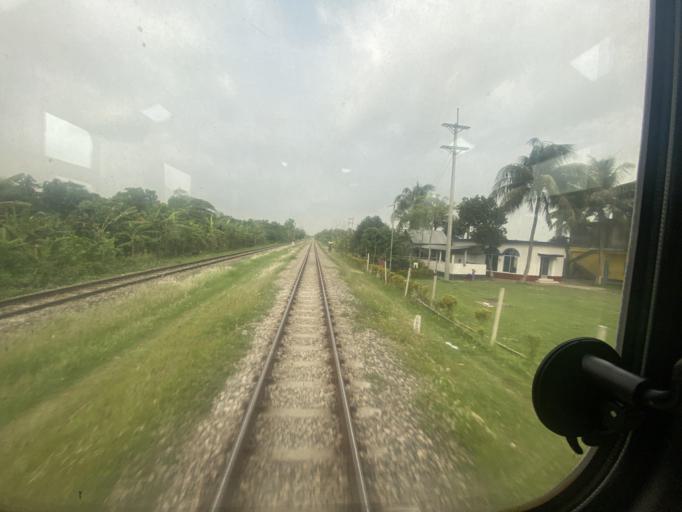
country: BD
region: Dhaka
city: Tungi
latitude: 23.9302
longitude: 90.5375
